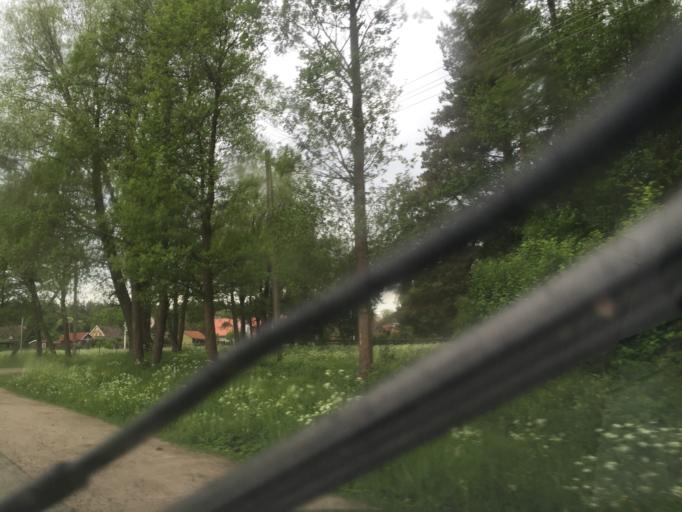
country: LT
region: Klaipedos apskritis
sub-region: Klaipeda
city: Palanga
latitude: 55.8162
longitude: 21.0714
